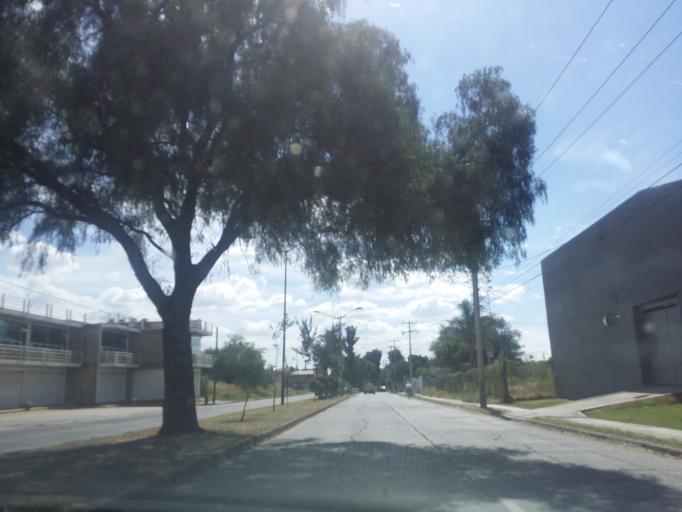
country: MX
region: Guanajuato
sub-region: Leon
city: Medina
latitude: 21.1572
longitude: -101.6441
